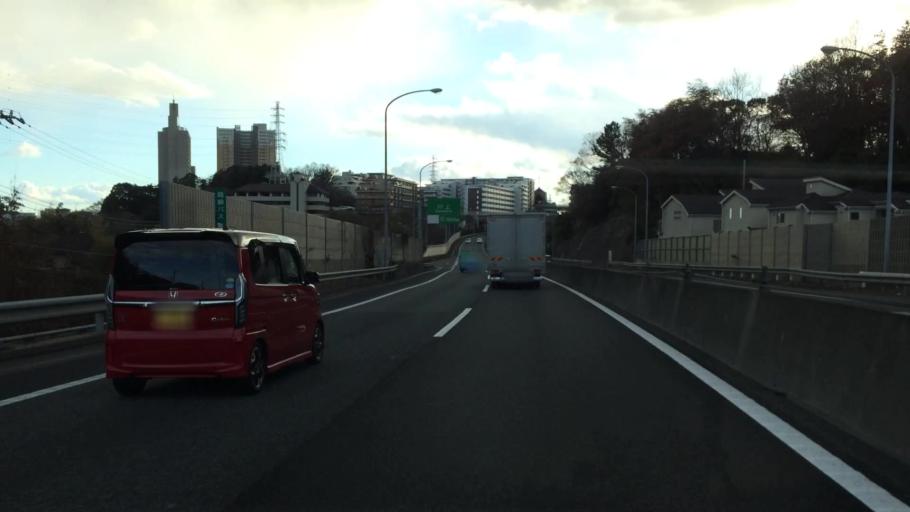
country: JP
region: Kanagawa
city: Yokohama
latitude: 35.4377
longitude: 139.5554
